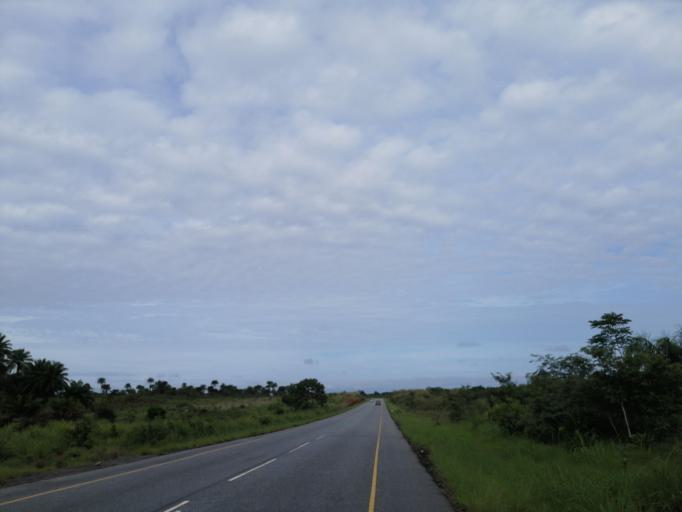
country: SL
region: Northern Province
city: Port Loko
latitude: 8.7843
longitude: -12.8503
